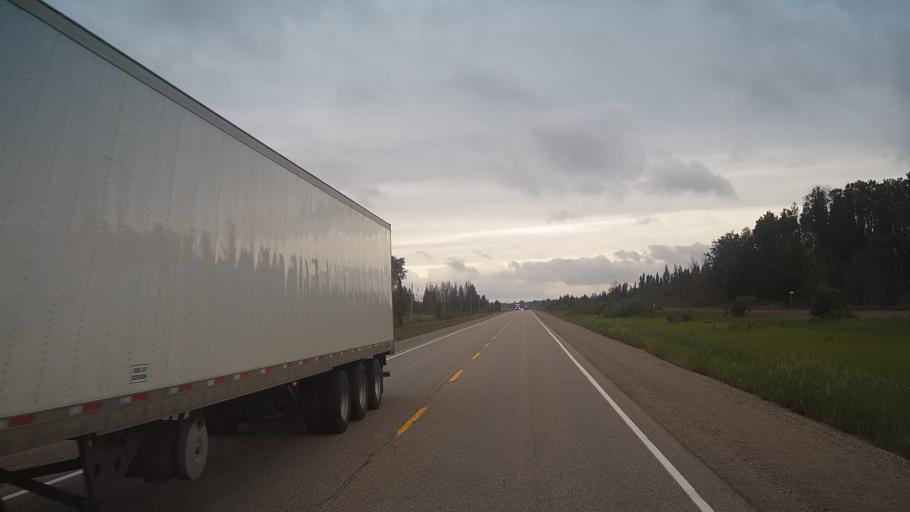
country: CA
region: Ontario
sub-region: Thunder Bay District
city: Thunder Bay
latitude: 48.8673
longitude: -89.9715
